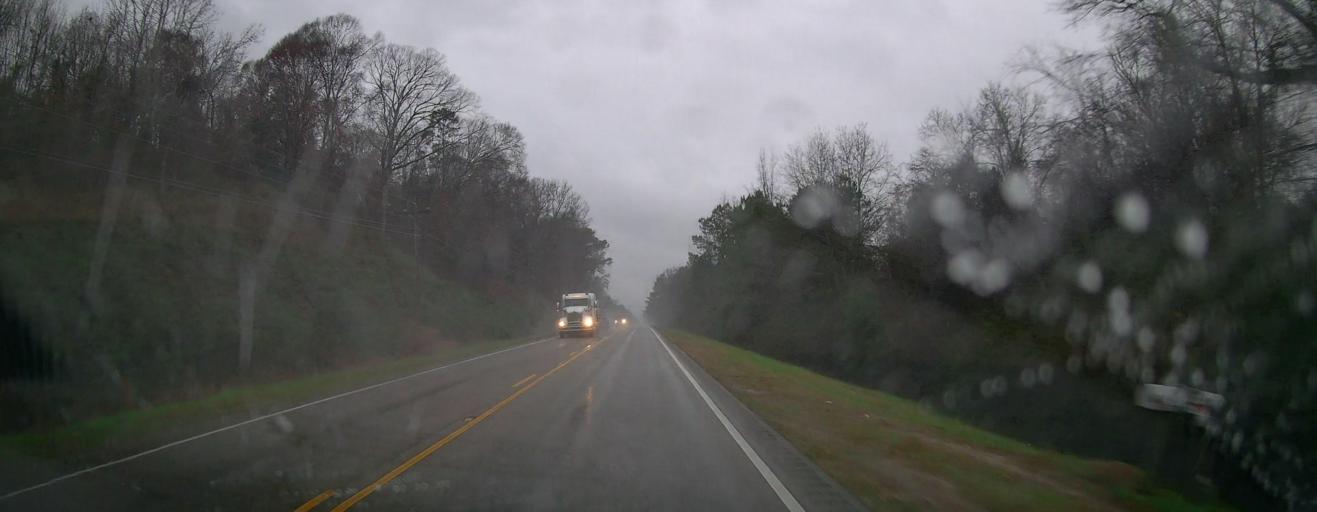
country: US
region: Alabama
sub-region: Autauga County
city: Prattville
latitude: 32.4768
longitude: -86.5251
